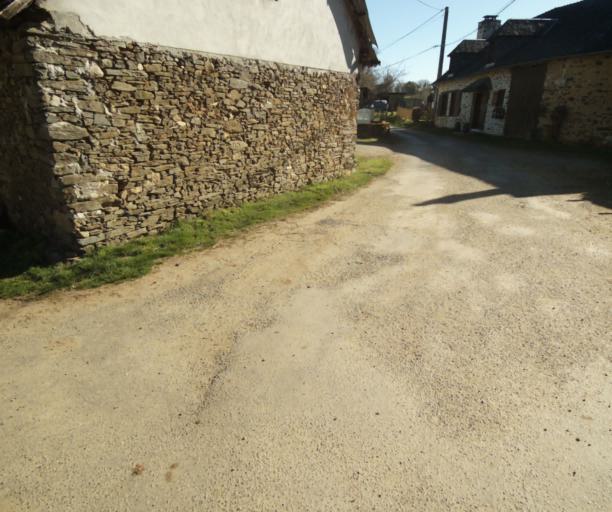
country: FR
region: Limousin
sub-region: Departement de la Correze
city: Chamboulive
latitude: 45.4114
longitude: 1.6557
